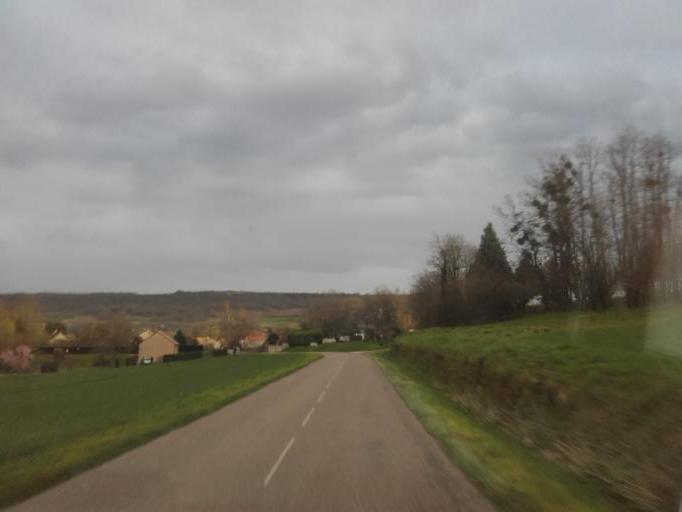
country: FR
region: Bourgogne
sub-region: Departement de Saone-et-Loire
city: Saint-Leger-sur-Dheune
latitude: 46.8993
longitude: 4.6636
